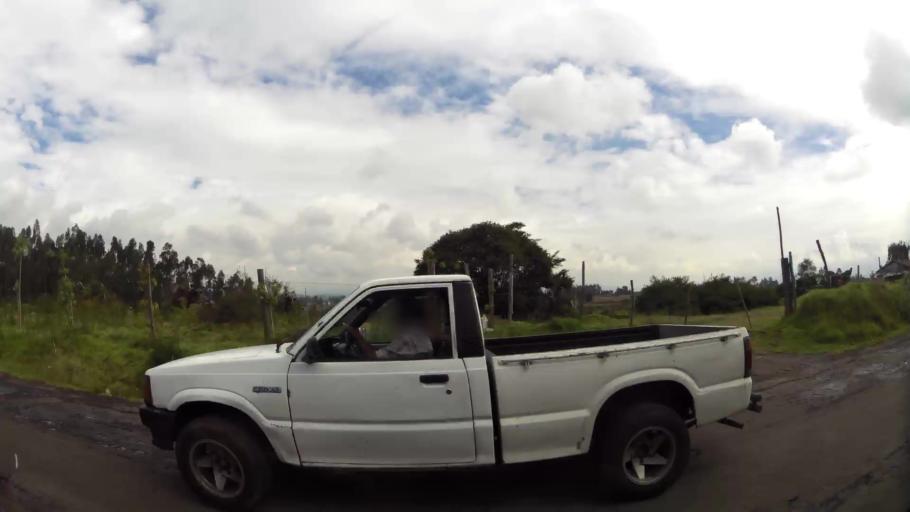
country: EC
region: Pichincha
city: Sangolqui
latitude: -0.3157
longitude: -78.4054
